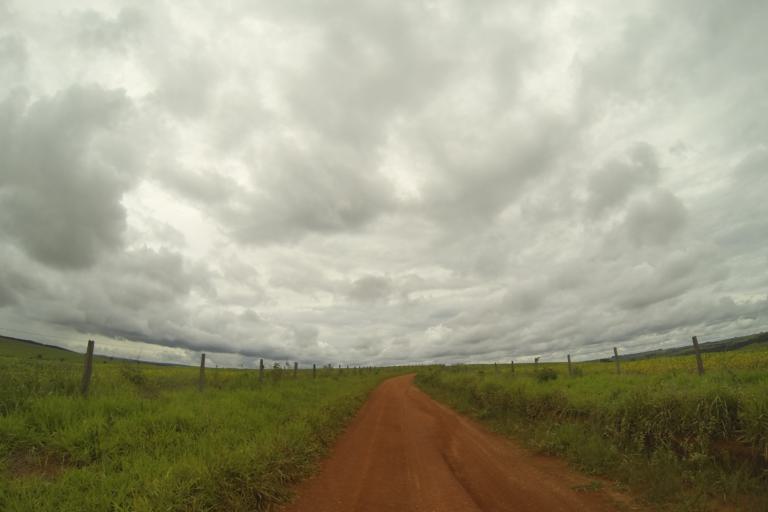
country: BR
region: Minas Gerais
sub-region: Ibia
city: Ibia
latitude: -19.7273
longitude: -46.5624
